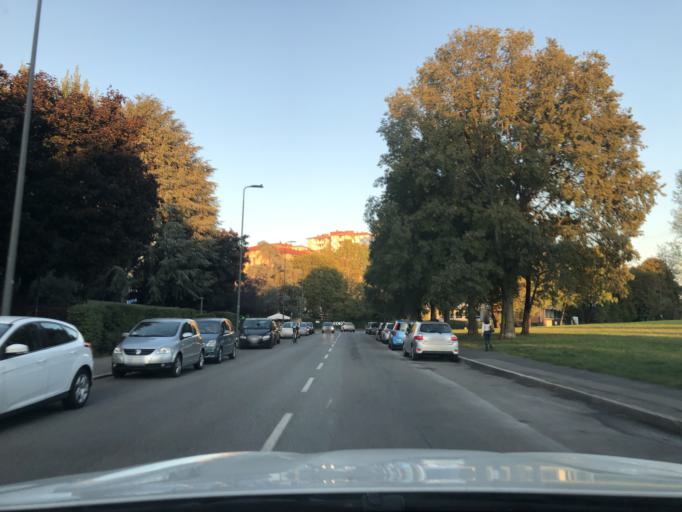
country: IT
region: Lombardy
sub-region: Citta metropolitana di Milano
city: Baranzate
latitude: 45.4942
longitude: 9.1229
